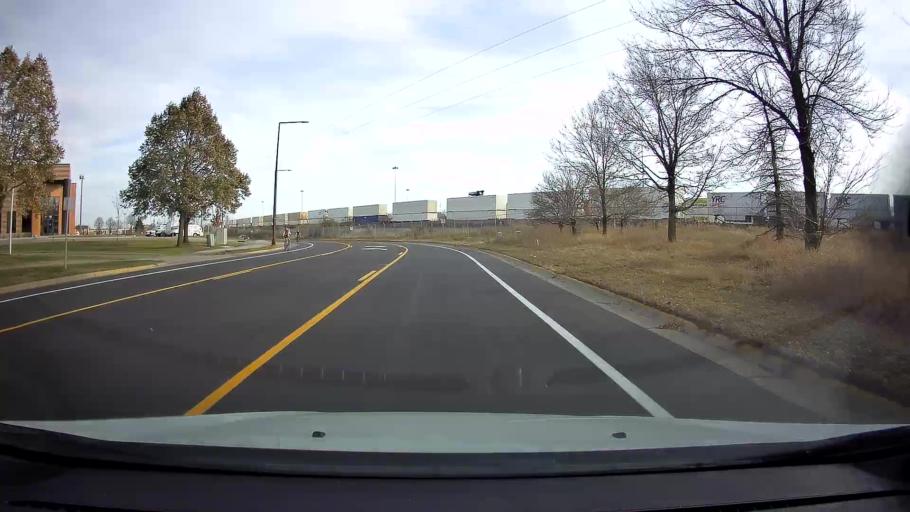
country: US
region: Minnesota
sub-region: Ramsey County
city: Falcon Heights
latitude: 44.9721
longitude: -93.1778
